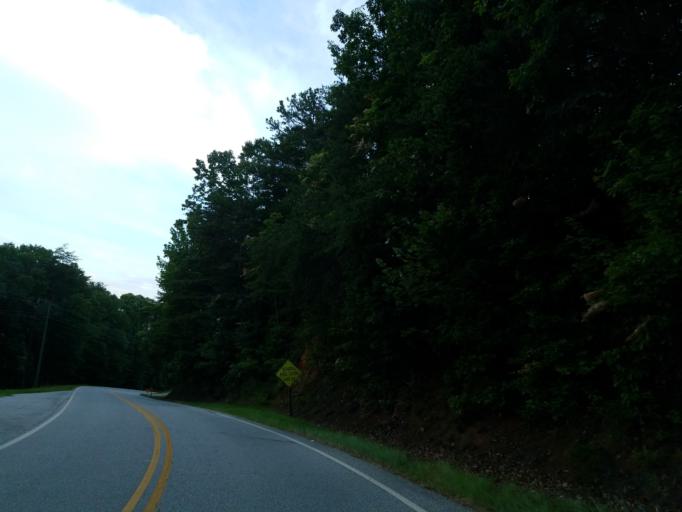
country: US
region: Georgia
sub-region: Lumpkin County
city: Dahlonega
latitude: 34.6029
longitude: -83.9700
